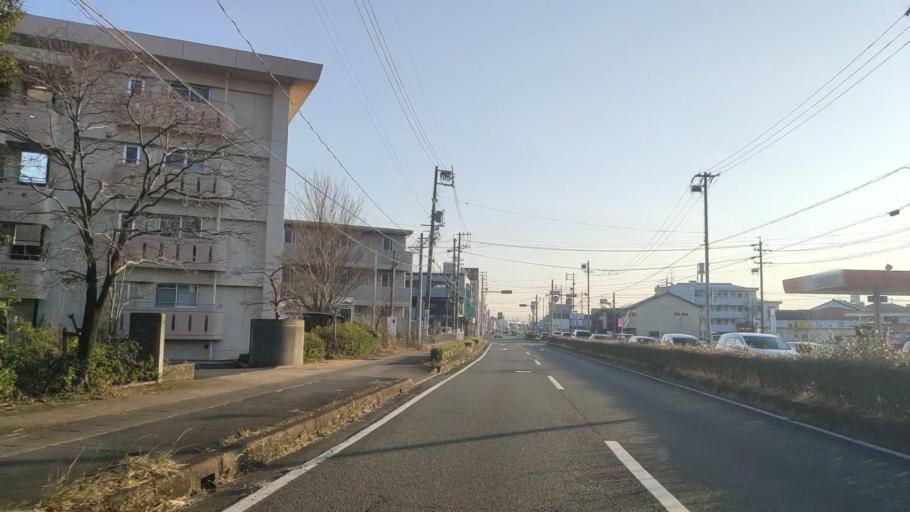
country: JP
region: Gifu
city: Gifu-shi
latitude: 35.4363
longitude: 136.7372
